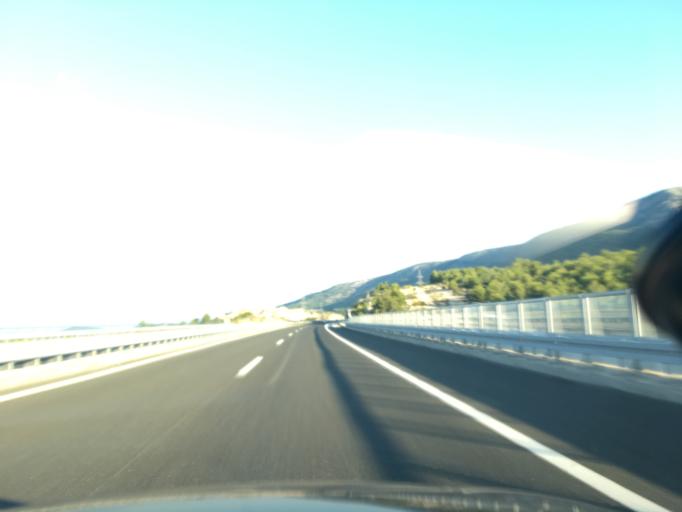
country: HR
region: Sibensko-Kniniska
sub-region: Grad Sibenik
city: Sibenik
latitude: 43.7344
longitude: 15.9709
